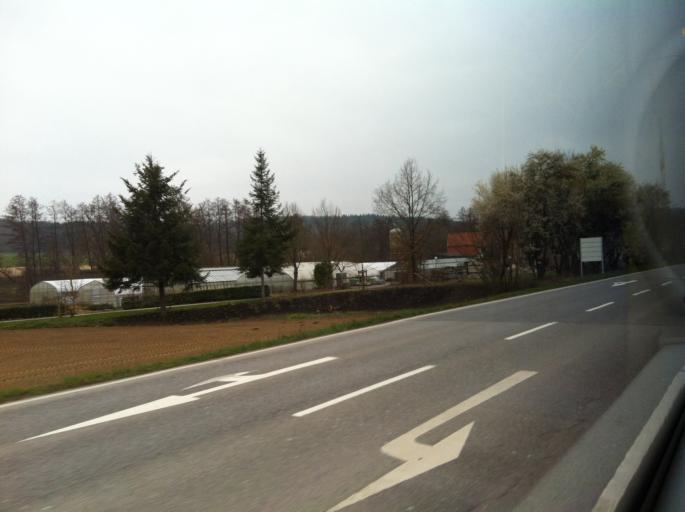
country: DE
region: Baden-Wuerttemberg
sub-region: Karlsruhe Region
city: Mosbach
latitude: 49.3666
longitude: 9.1527
